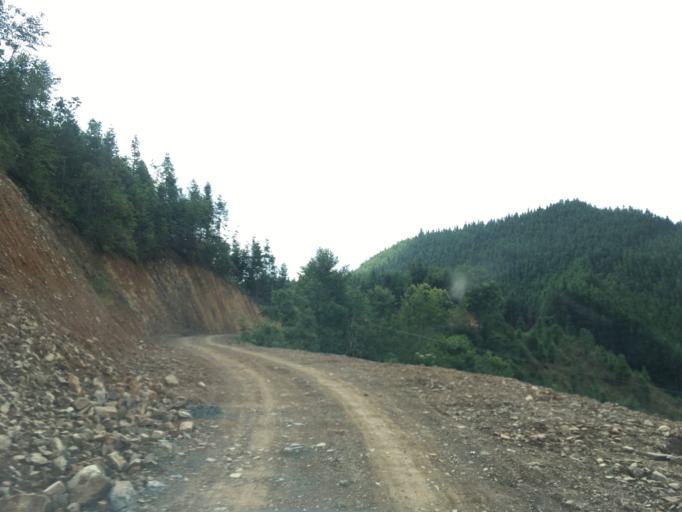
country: CN
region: Guangxi Zhuangzu Zizhiqu
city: Xinzhou
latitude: 24.8693
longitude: 105.8472
